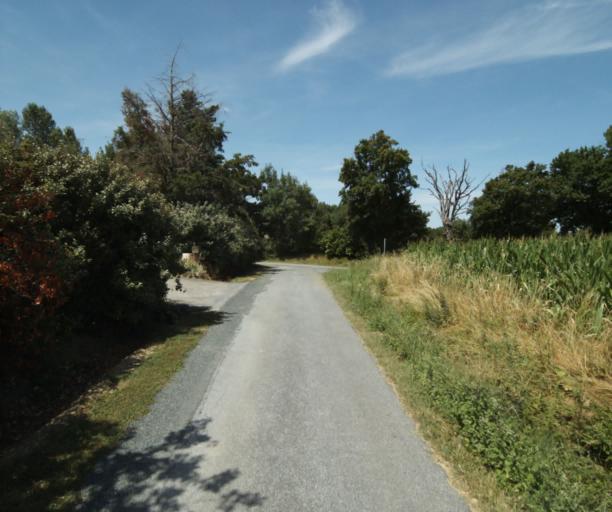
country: FR
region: Midi-Pyrenees
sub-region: Departement du Tarn
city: Soreze
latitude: 43.4916
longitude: 2.0590
